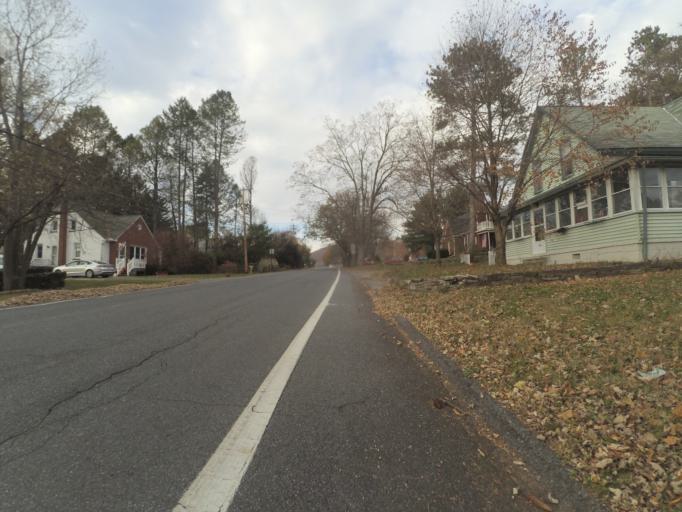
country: US
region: Pennsylvania
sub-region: Centre County
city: Boalsburg
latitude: 40.7845
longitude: -77.7945
